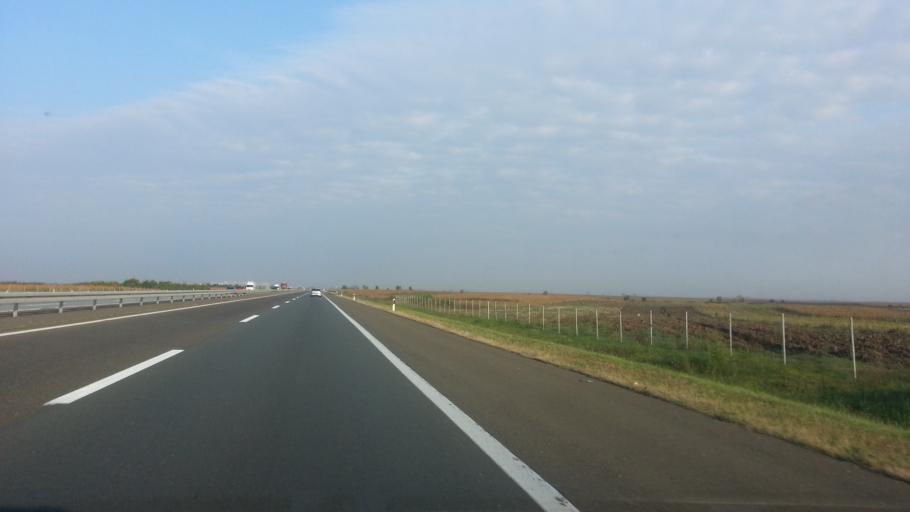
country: RS
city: Novi Banovci
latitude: 44.9536
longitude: 20.2634
